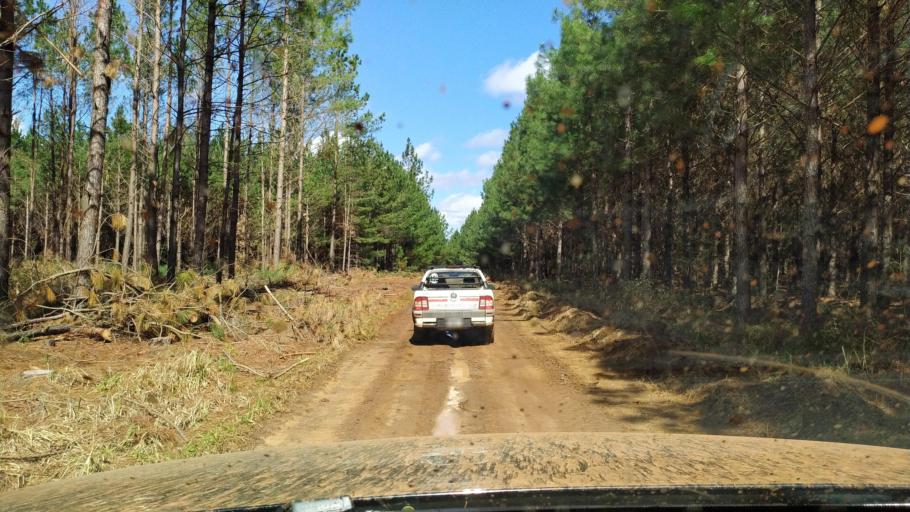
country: AR
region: Corrientes
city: Santo Tome
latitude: -28.4077
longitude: -56.0162
